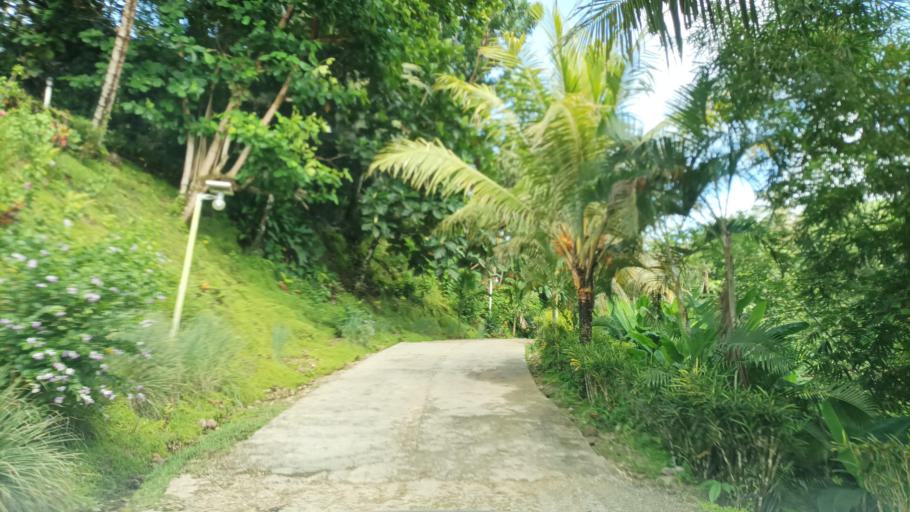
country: FM
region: Pohnpei
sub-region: Kolonia Municipality
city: Kolonia Town
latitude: 6.9606
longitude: 158.2054
